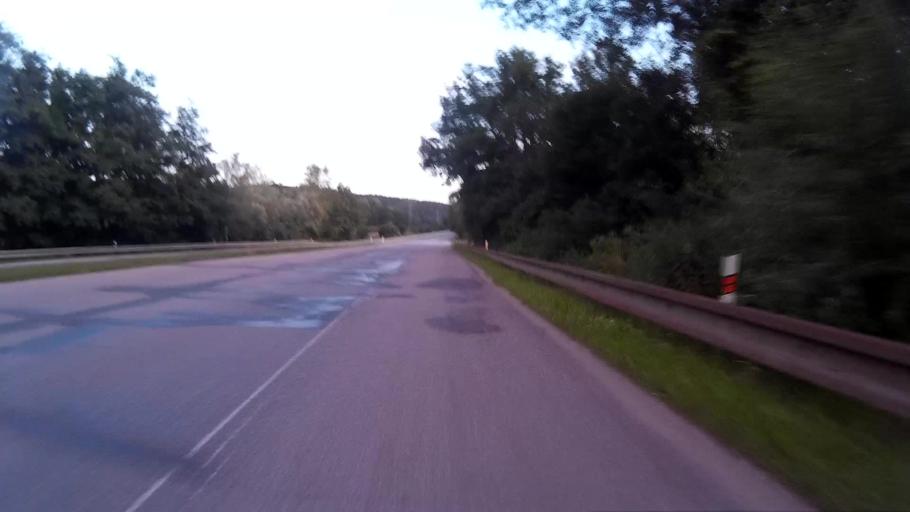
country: CZ
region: South Moravian
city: Troubsko
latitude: 49.2124
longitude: 16.5216
